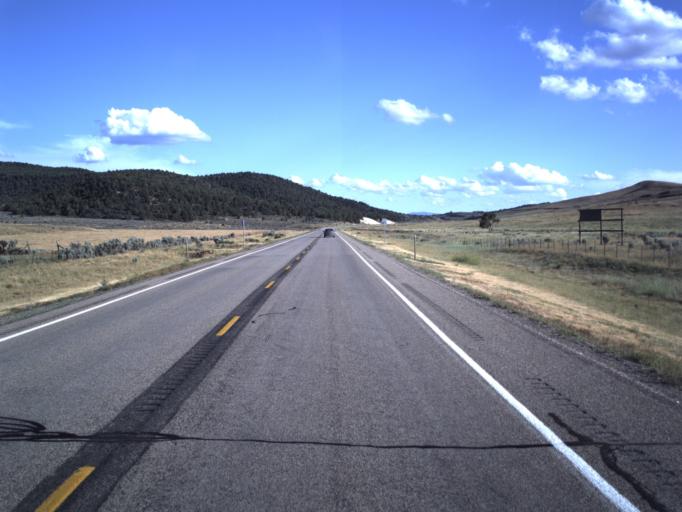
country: US
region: Utah
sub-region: Sanpete County
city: Fairview
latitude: 39.7548
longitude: -111.4803
